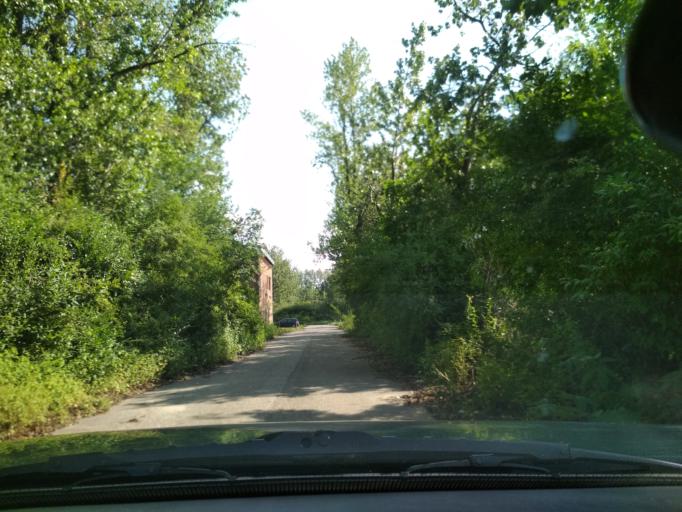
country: PL
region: Silesian Voivodeship
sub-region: Gliwice
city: Gliwice
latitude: 50.2757
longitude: 18.6874
